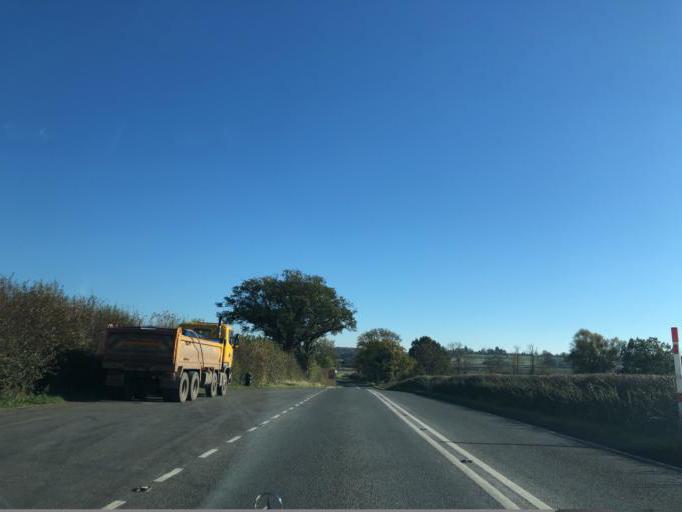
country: GB
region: England
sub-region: Warwickshire
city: Harbury
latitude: 52.2655
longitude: -1.4665
